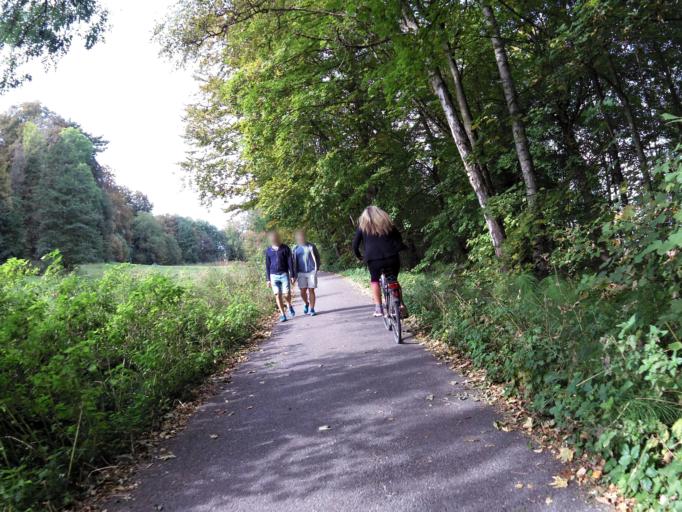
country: DE
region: Bavaria
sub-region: Upper Bavaria
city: Bernried
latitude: 47.8635
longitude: 11.2995
